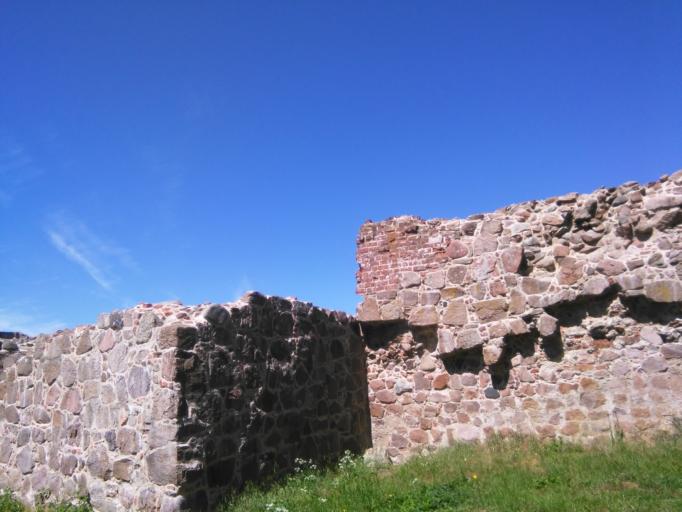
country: DK
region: Capital Region
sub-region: Bornholm Kommune
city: Ronne
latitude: 55.2711
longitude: 14.7544
